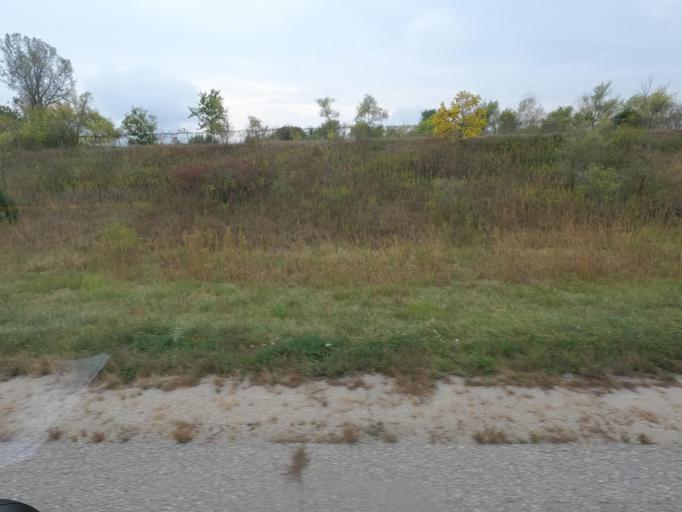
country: US
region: Iowa
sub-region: Wapello County
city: Eddyville
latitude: 41.1671
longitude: -92.6255
